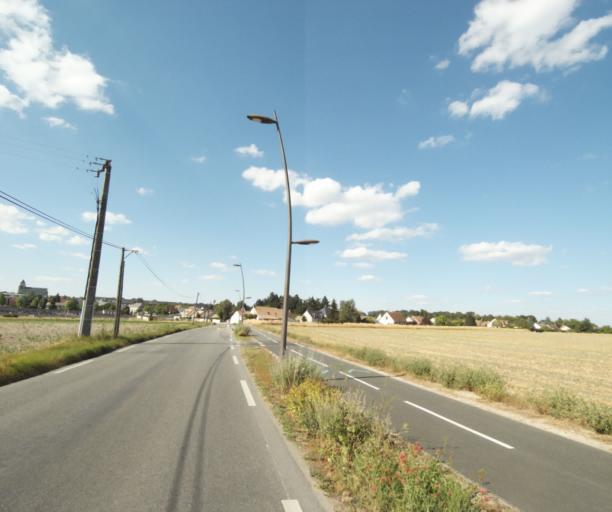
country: FR
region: Centre
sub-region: Departement du Loiret
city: Ingre
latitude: 47.9137
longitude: 1.8302
